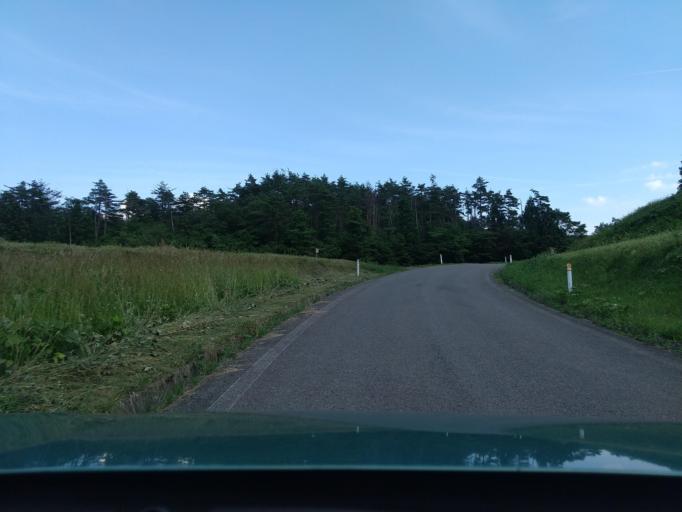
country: JP
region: Iwate
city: Ichinoseki
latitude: 39.0082
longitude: 141.2247
